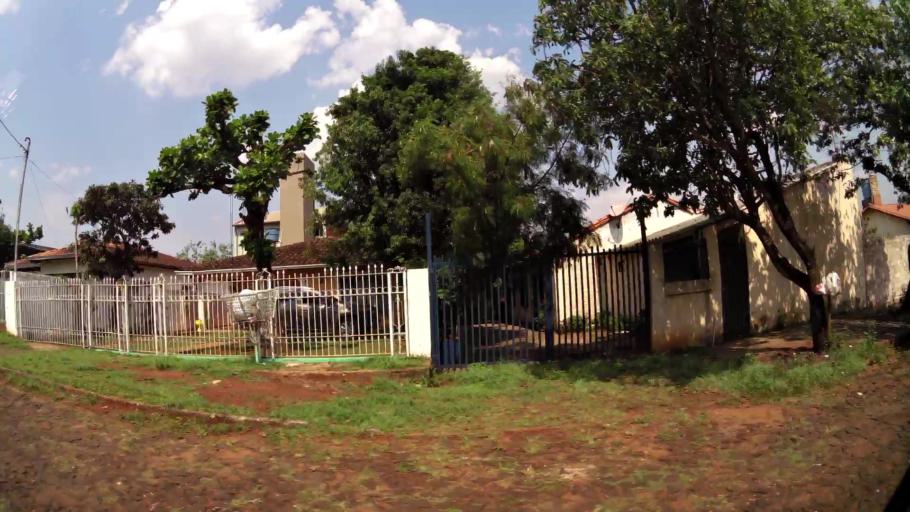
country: PY
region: Alto Parana
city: Ciudad del Este
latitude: -25.5112
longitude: -54.6365
